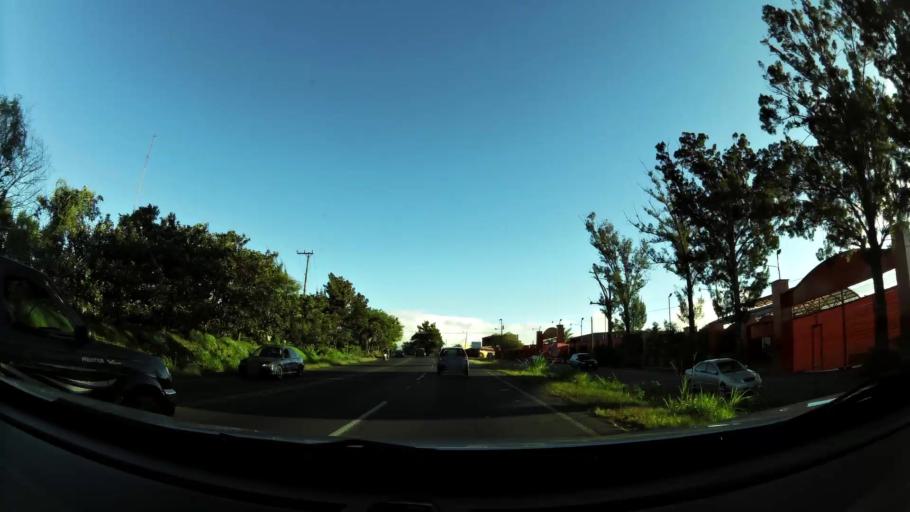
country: CR
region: Heredia
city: Angeles
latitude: 9.9817
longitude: -84.0477
